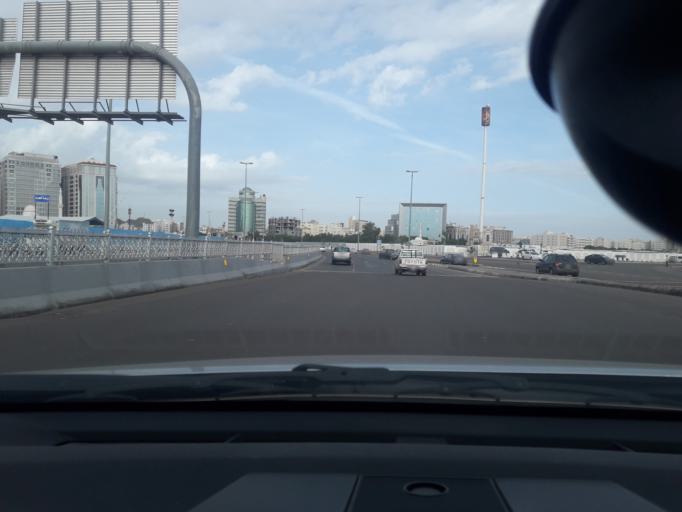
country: SA
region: Al Madinah al Munawwarah
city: Medina
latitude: 24.4719
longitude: 39.6180
